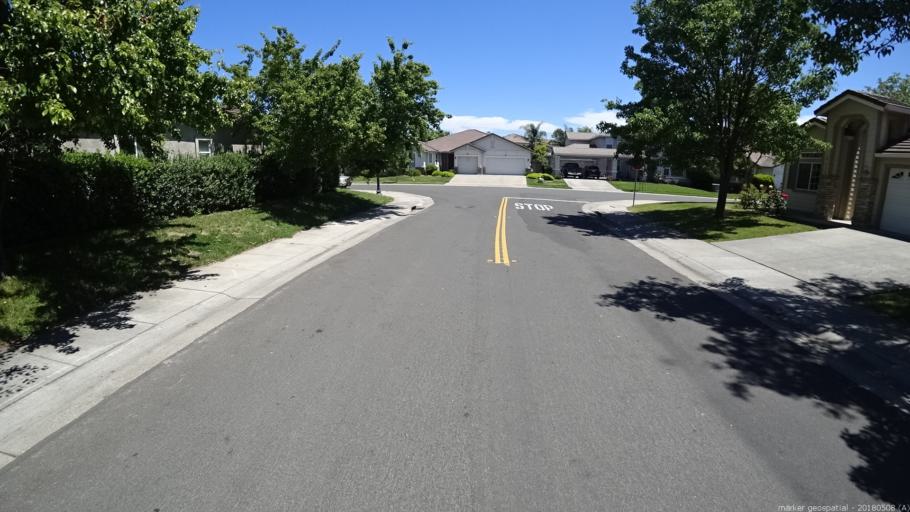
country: US
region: California
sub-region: Sacramento County
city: Elverta
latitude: 38.6773
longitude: -121.5257
